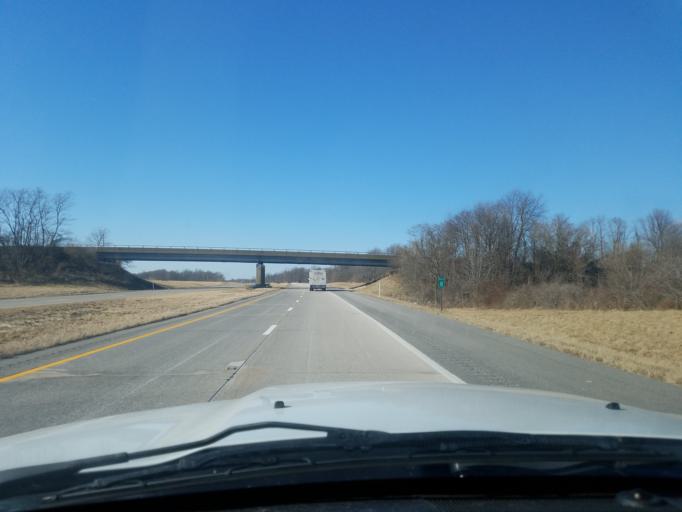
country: US
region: Kentucky
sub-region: Henderson County
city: Henderson
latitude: 37.7695
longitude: -87.4282
